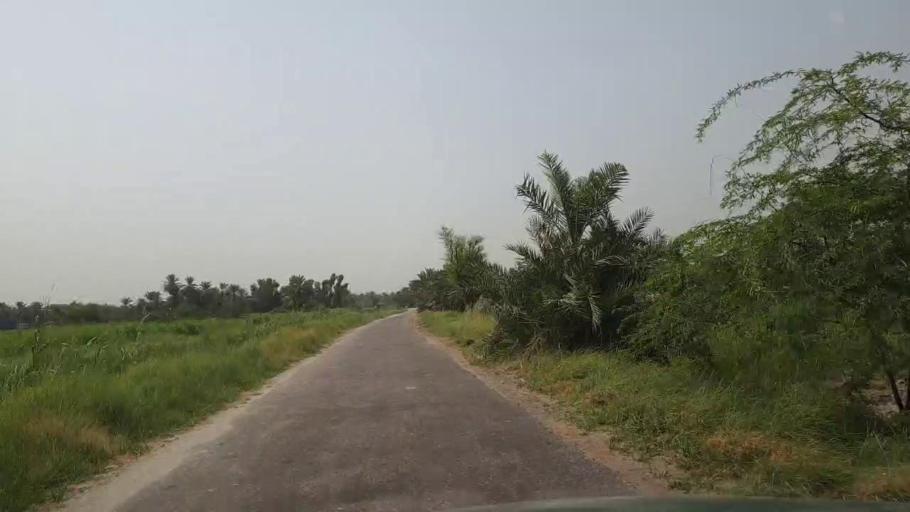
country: PK
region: Sindh
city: Gambat
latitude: 27.3813
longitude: 68.5482
